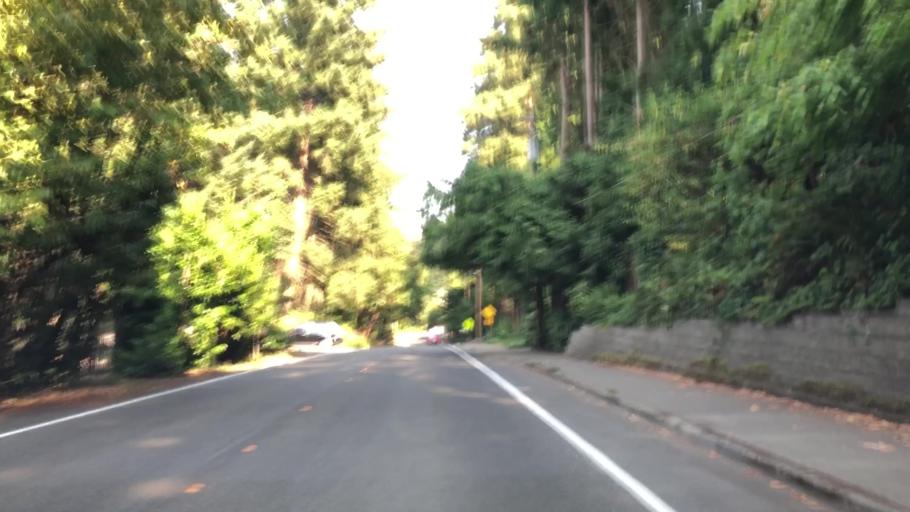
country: US
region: Washington
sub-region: King County
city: Bellevue
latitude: 47.5881
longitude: -122.1994
